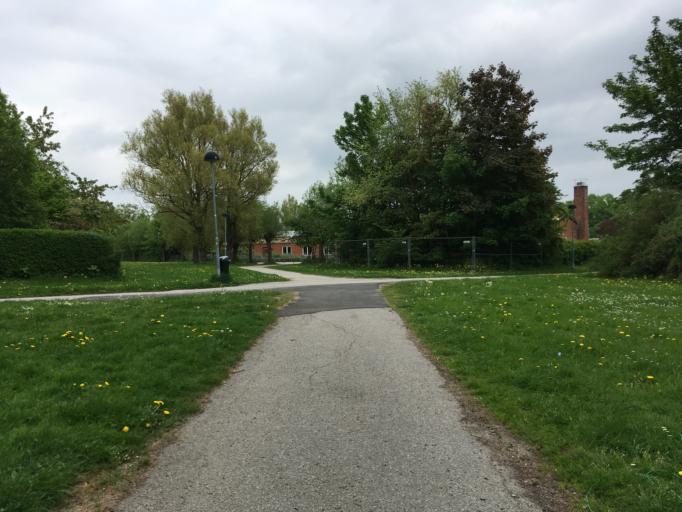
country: SE
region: Skane
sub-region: Lunds Kommun
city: Lund
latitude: 55.6999
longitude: 13.1699
